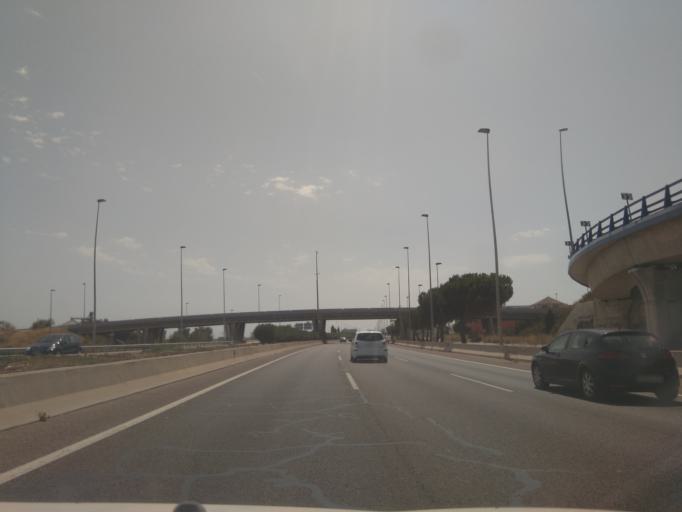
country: ES
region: Valencia
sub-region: Provincia de Valencia
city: Alfafar
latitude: 39.4125
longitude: -0.3792
